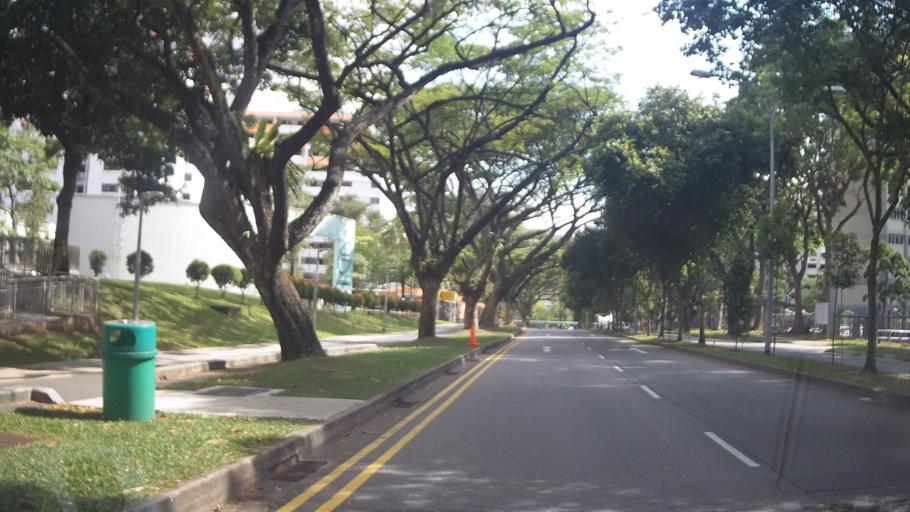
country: SG
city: Singapore
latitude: 1.3197
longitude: 103.7664
